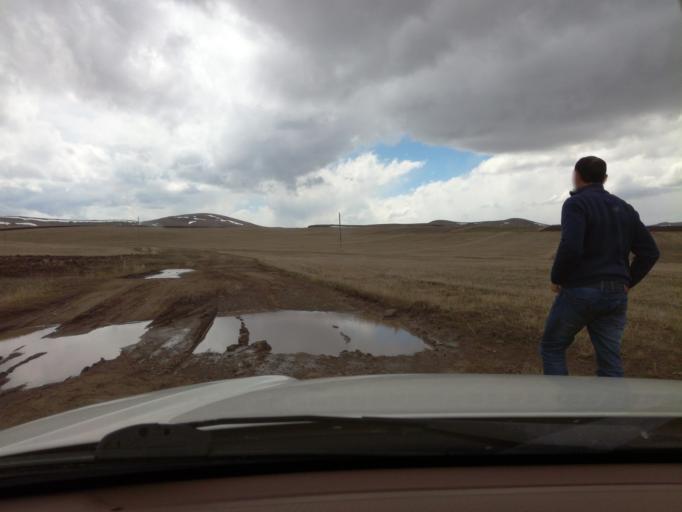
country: AM
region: Shirak
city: Amasia
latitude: 41.0257
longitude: 43.8225
